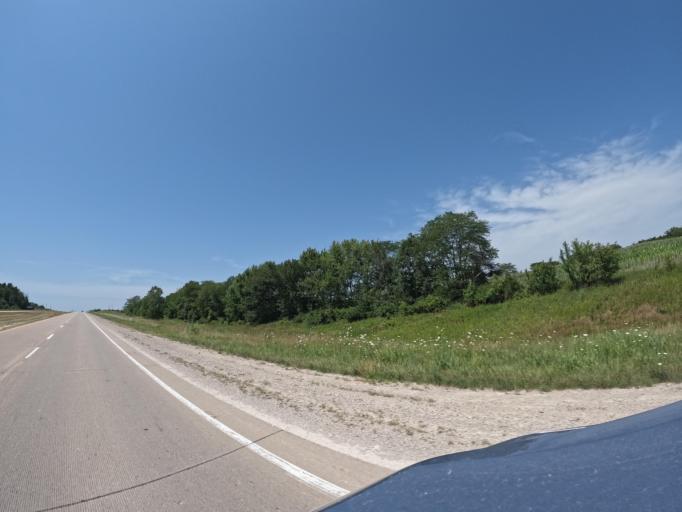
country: US
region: Iowa
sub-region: Henry County
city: Mount Pleasant
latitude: 40.9735
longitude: -91.6544
